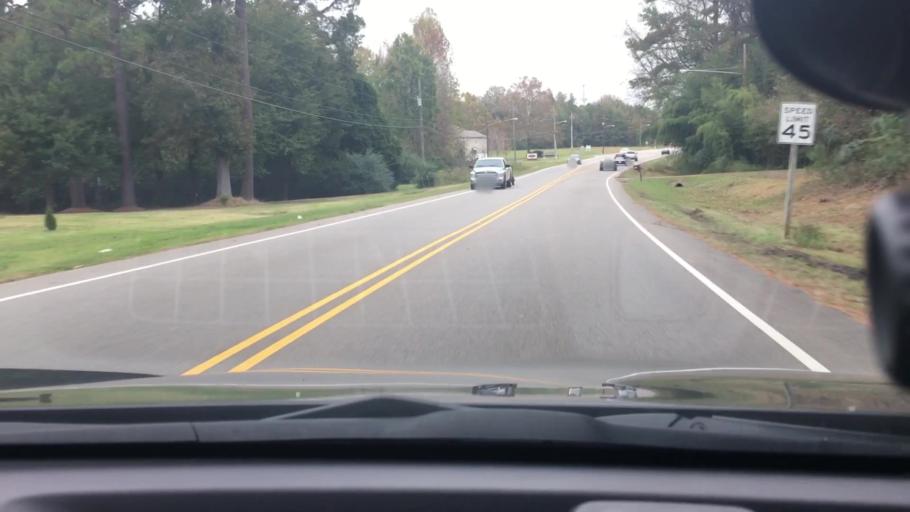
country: US
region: North Carolina
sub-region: Pitt County
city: Summerfield
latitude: 35.5892
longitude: -77.4088
